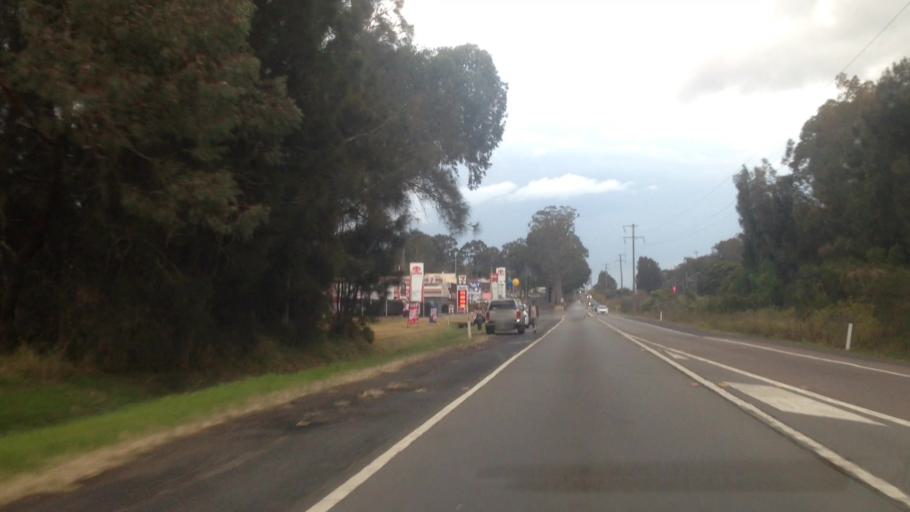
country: AU
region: New South Wales
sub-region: Wyong Shire
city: Jilliby
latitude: -33.2757
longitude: 151.4290
